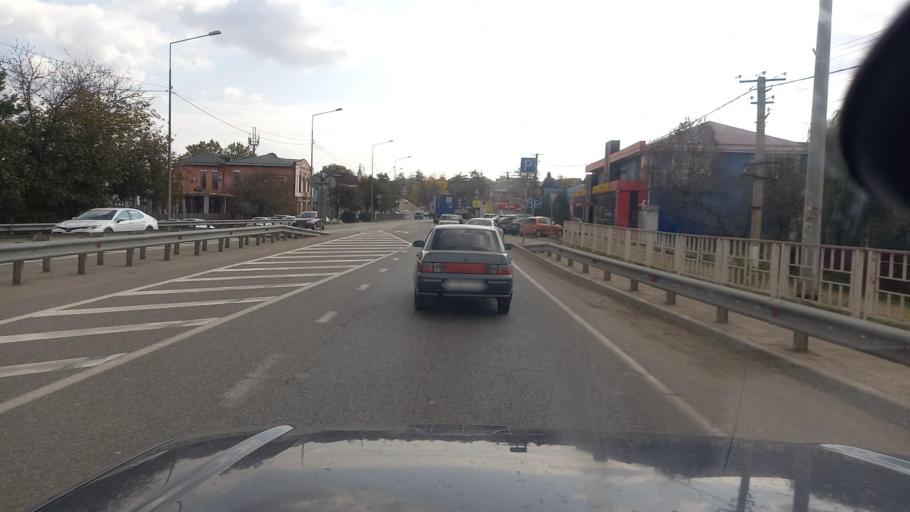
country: RU
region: Krasnodarskiy
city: Kholmskiy
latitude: 44.8443
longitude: 38.3916
